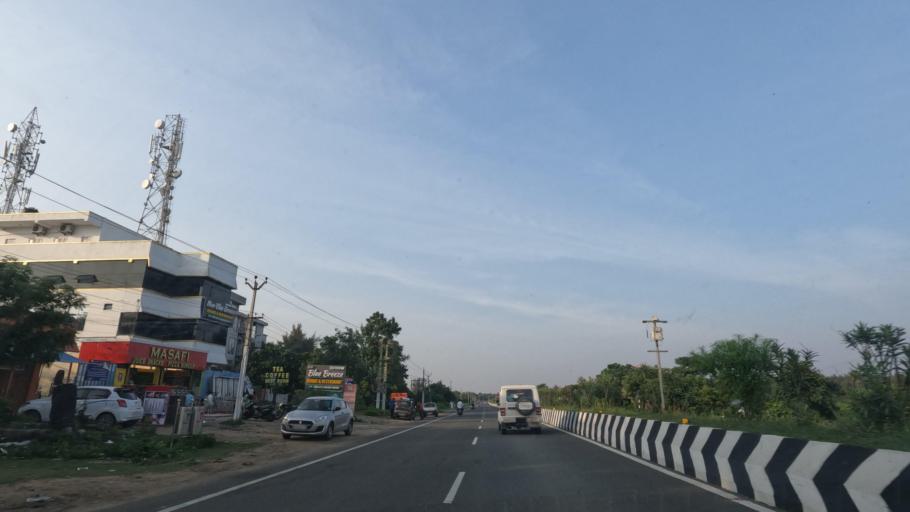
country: IN
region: Tamil Nadu
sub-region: Kancheepuram
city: Mamallapuram
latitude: 12.6619
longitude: 80.2092
